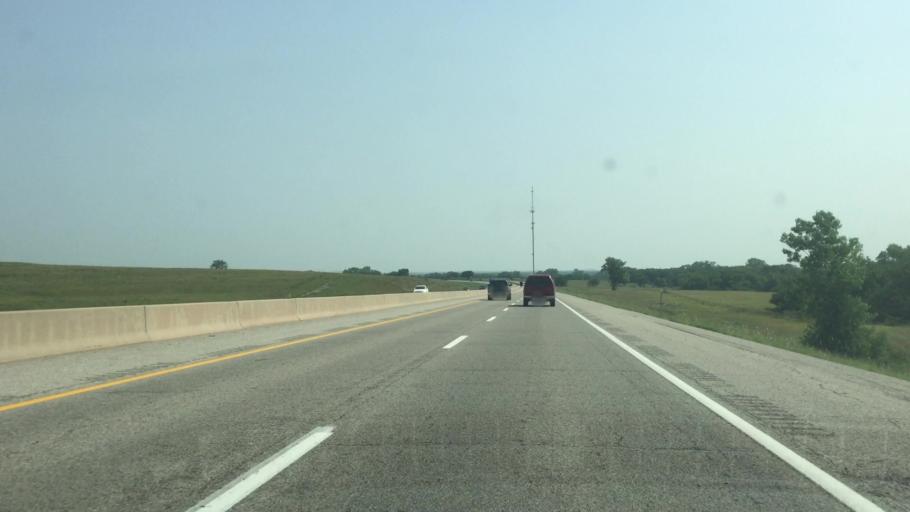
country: US
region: Kansas
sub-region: Lyon County
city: Emporia
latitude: 38.3284
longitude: -96.3106
